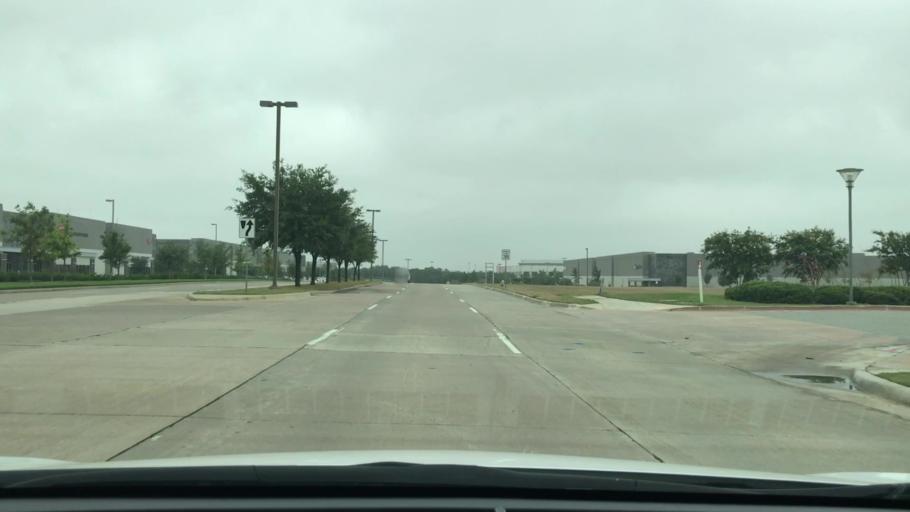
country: US
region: Texas
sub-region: Dallas County
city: Coppell
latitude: 32.9149
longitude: -96.9988
